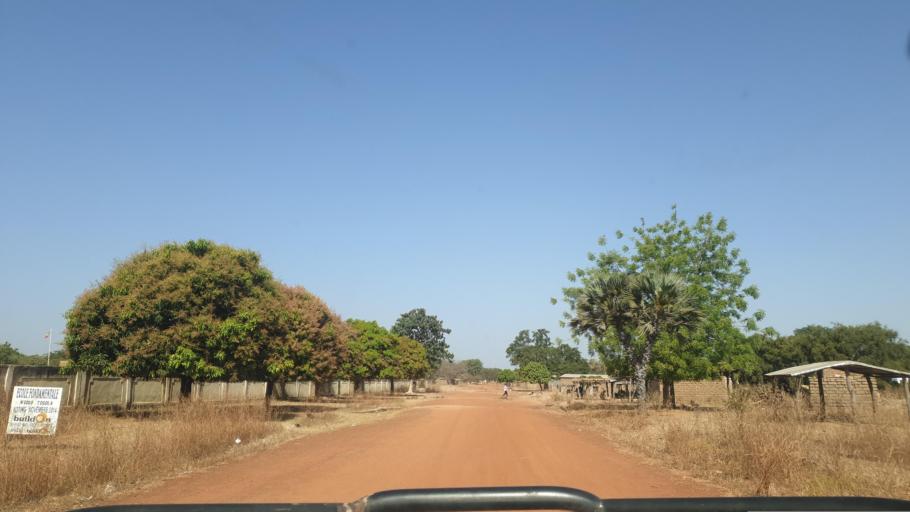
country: ML
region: Sikasso
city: Bougouni
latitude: 11.8126
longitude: -6.9348
